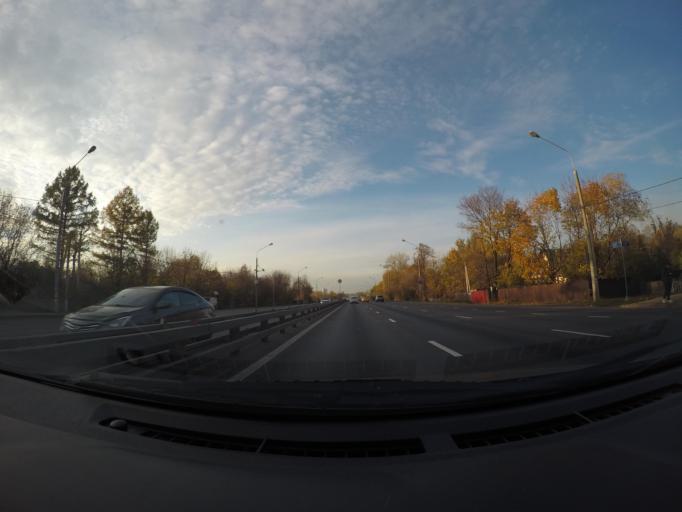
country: RU
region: Moskovskaya
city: Novopodrezkovo
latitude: 55.9260
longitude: 37.3853
